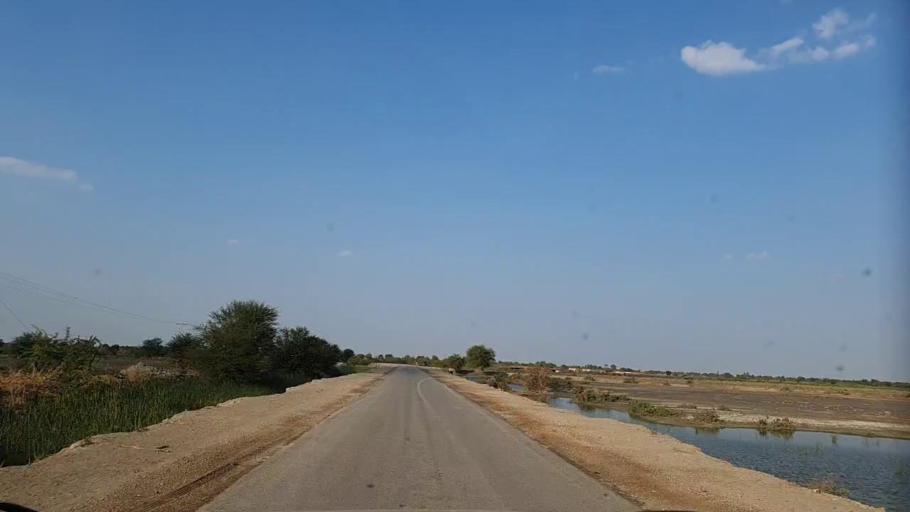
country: PK
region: Sindh
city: Pithoro
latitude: 25.6968
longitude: 69.2226
